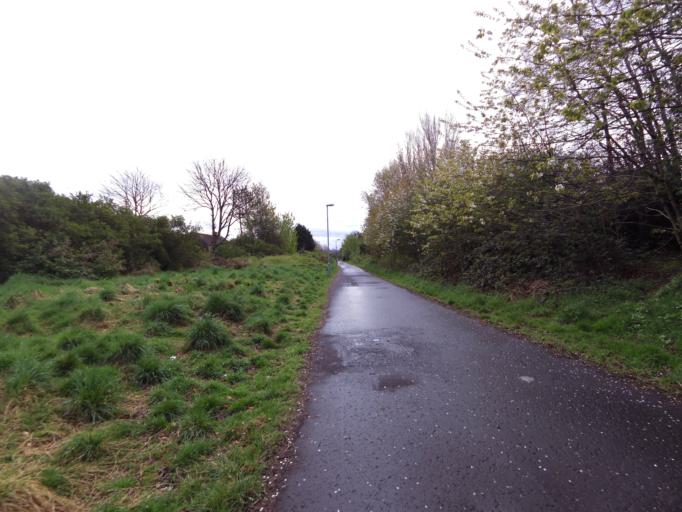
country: GB
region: Scotland
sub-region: Edinburgh
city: Colinton
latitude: 55.9629
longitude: -3.2557
